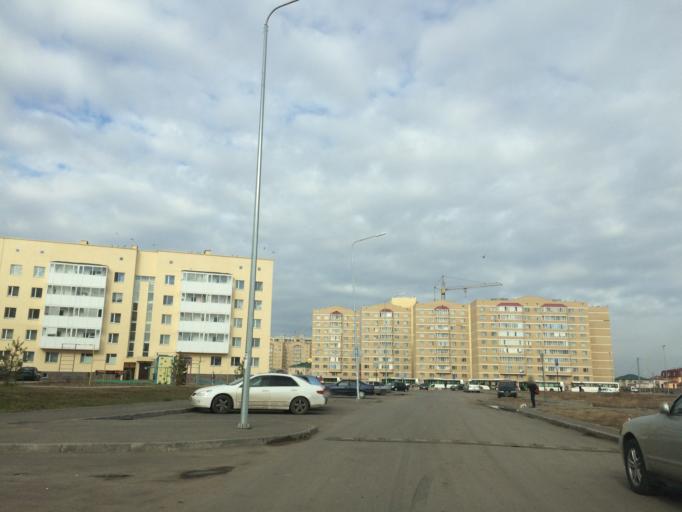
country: KZ
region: Astana Qalasy
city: Astana
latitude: 51.1700
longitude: 71.3737
